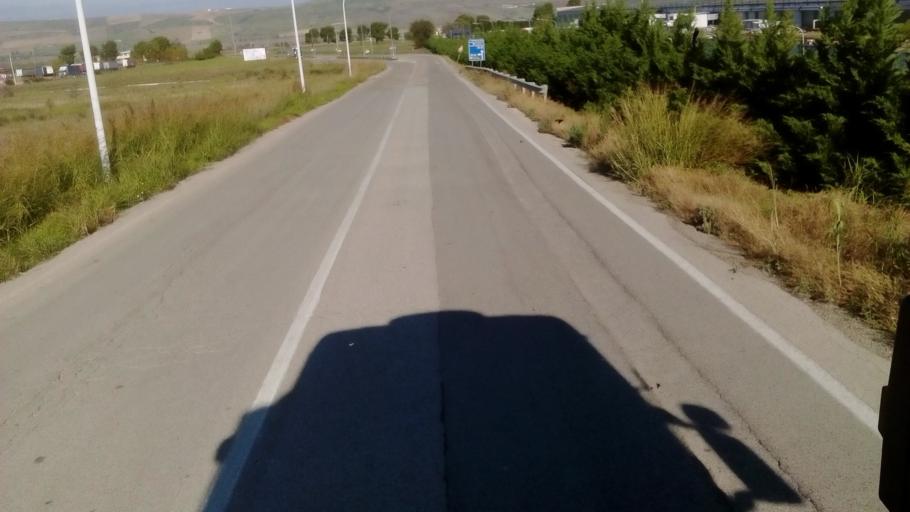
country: IT
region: Basilicate
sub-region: Provincia di Potenza
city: Melfi
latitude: 41.0733
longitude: 15.6910
